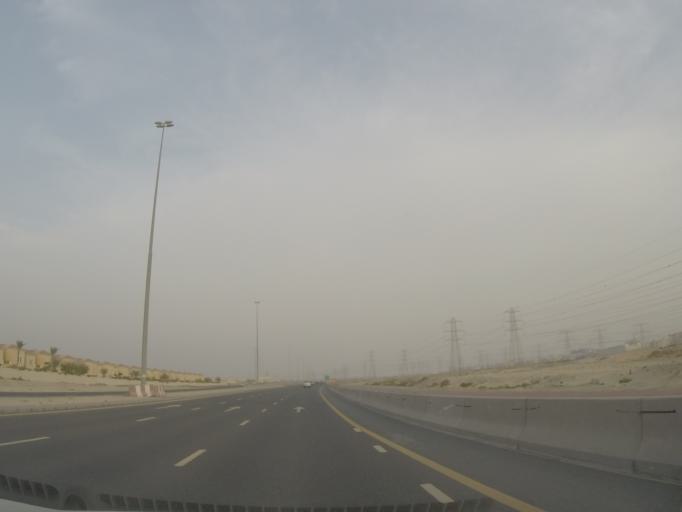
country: AE
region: Dubai
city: Dubai
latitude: 25.0446
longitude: 55.1511
